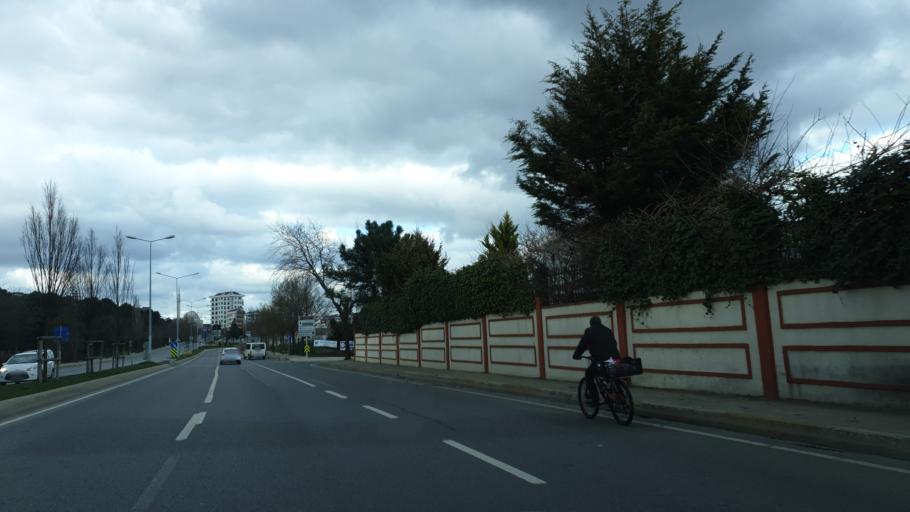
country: TR
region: Istanbul
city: Sultanbeyli
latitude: 40.9293
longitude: 29.2732
